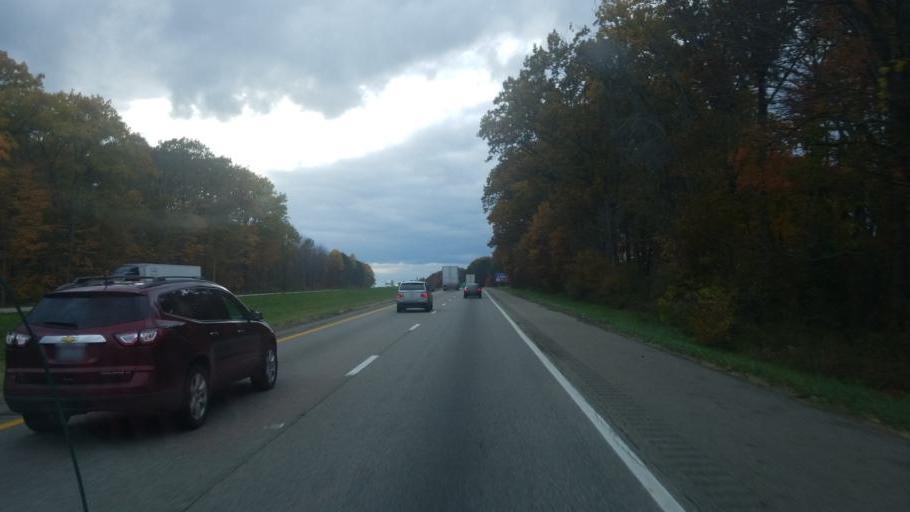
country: US
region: Ohio
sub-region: Trumbull County
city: Churchill
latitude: 41.1597
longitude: -80.6360
